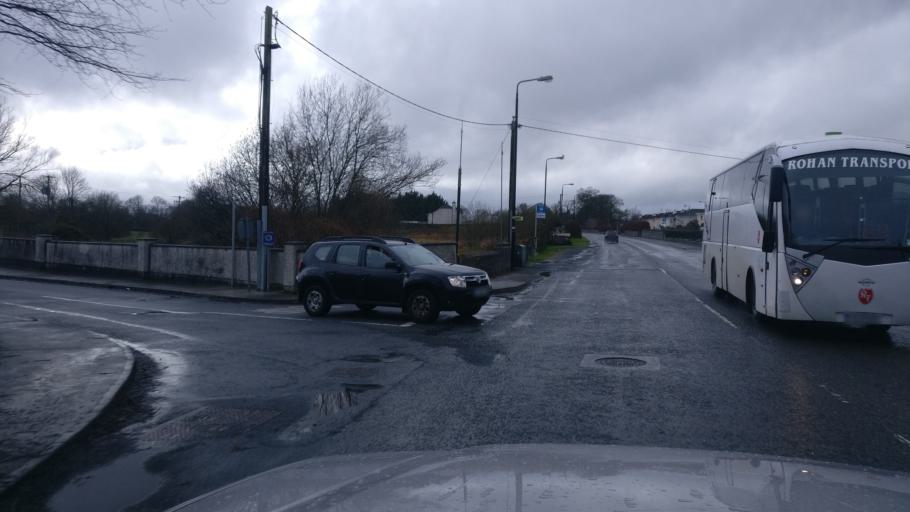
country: IE
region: Leinster
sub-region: An Iarmhi
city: Athlone
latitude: 53.4259
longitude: -8.0094
